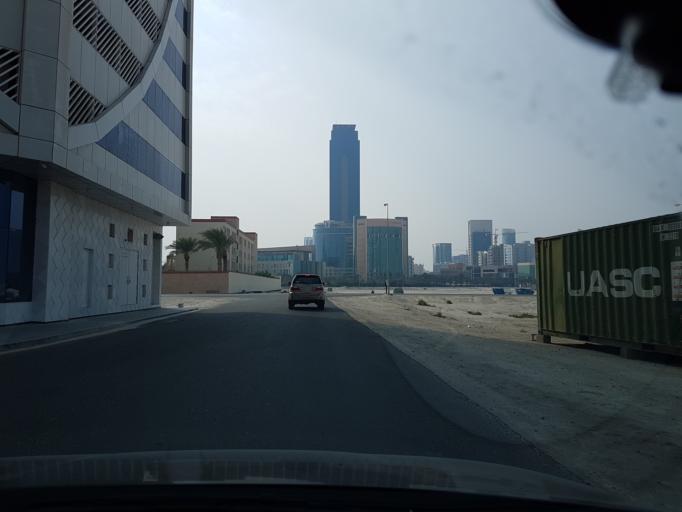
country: BH
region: Manama
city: Jidd Hafs
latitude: 26.2355
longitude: 50.5474
